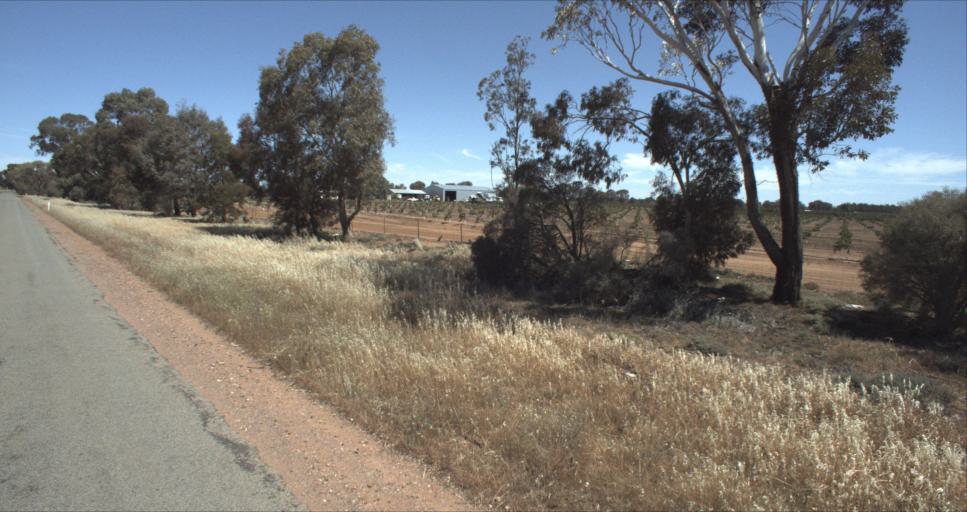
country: AU
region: New South Wales
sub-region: Leeton
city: Leeton
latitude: -34.5201
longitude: 146.3456
